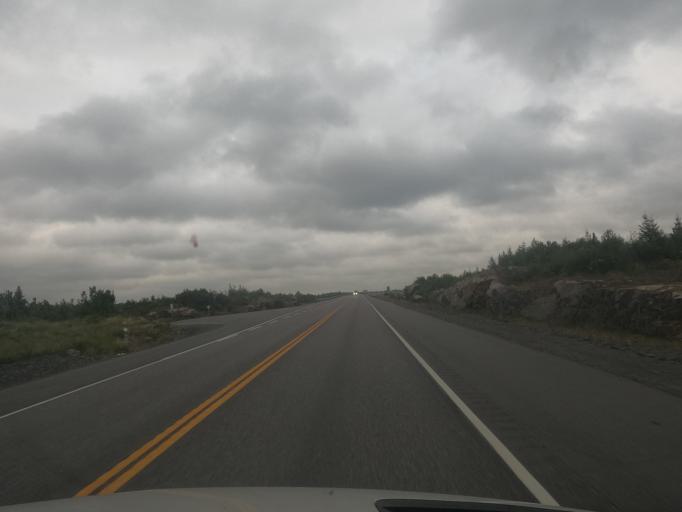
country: CA
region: Ontario
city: Greater Sudbury
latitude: 46.4328
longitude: -81.0210
